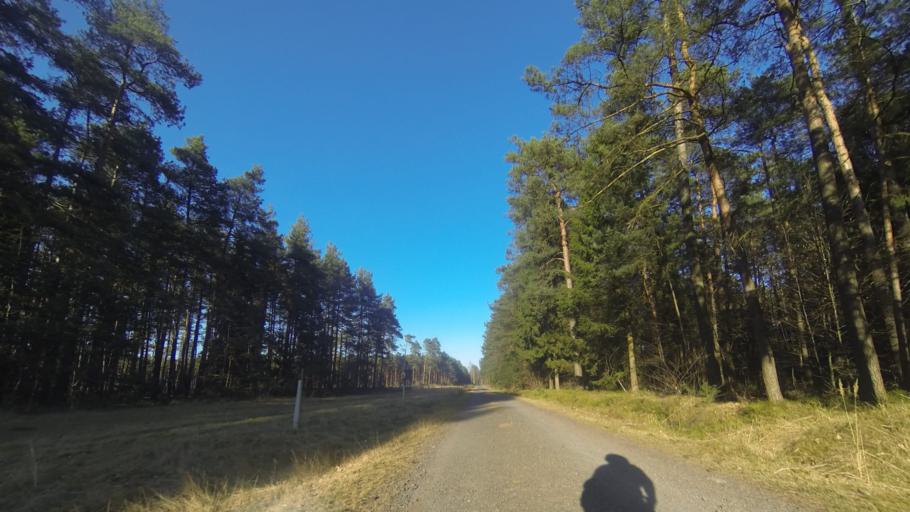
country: DE
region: Saxony
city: Tauscha
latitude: 51.2454
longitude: 13.8274
